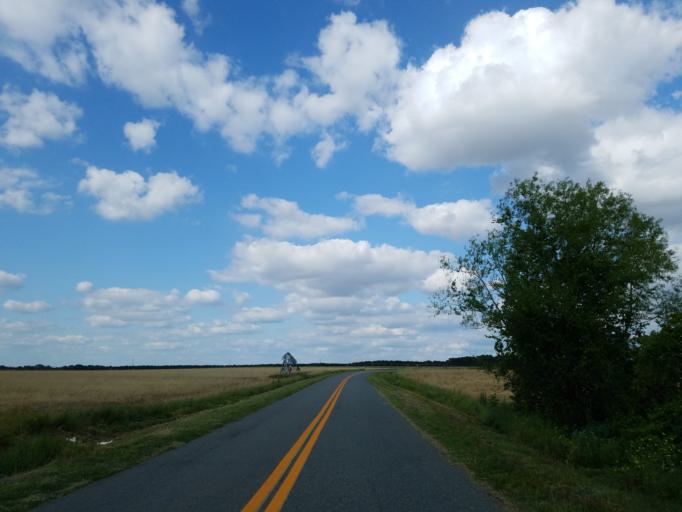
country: US
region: Georgia
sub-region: Dooly County
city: Unadilla
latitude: 32.1852
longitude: -83.7823
